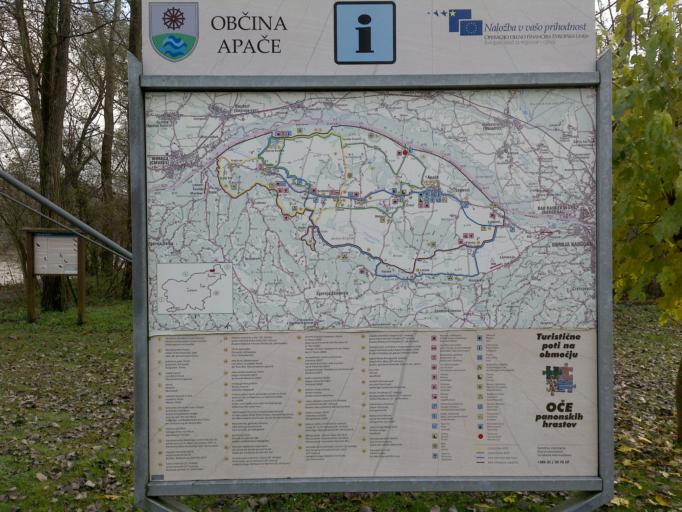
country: SI
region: Apace
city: Apace
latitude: 46.7134
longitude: 15.8928
